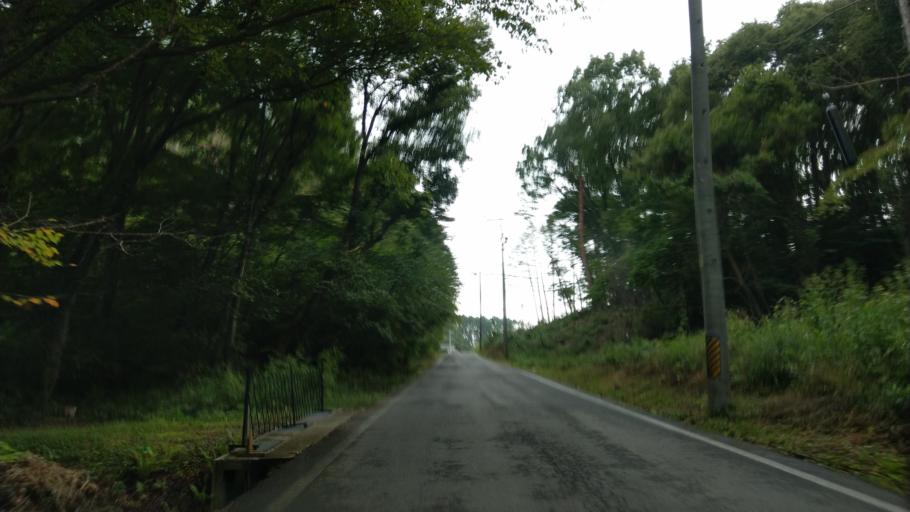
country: JP
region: Nagano
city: Komoro
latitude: 36.3065
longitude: 138.3910
